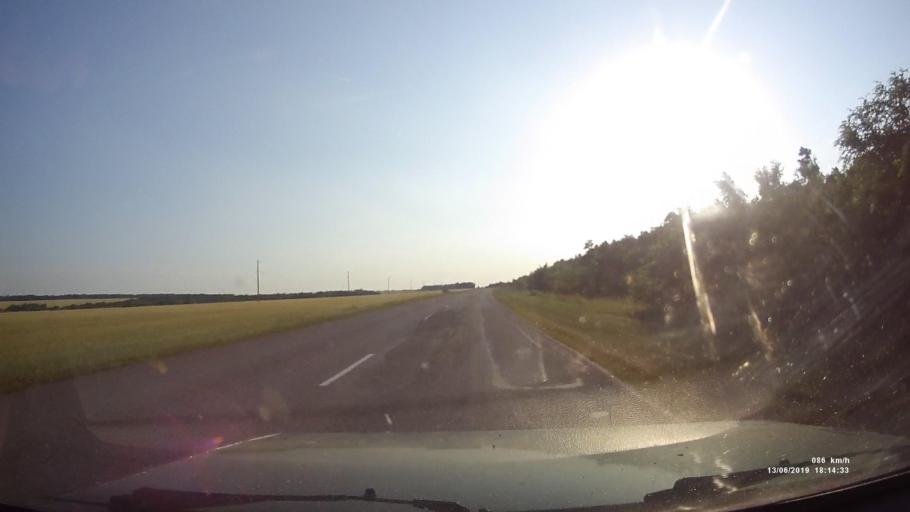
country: RU
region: Rostov
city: Kazanskaya
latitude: 49.9334
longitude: 41.3743
